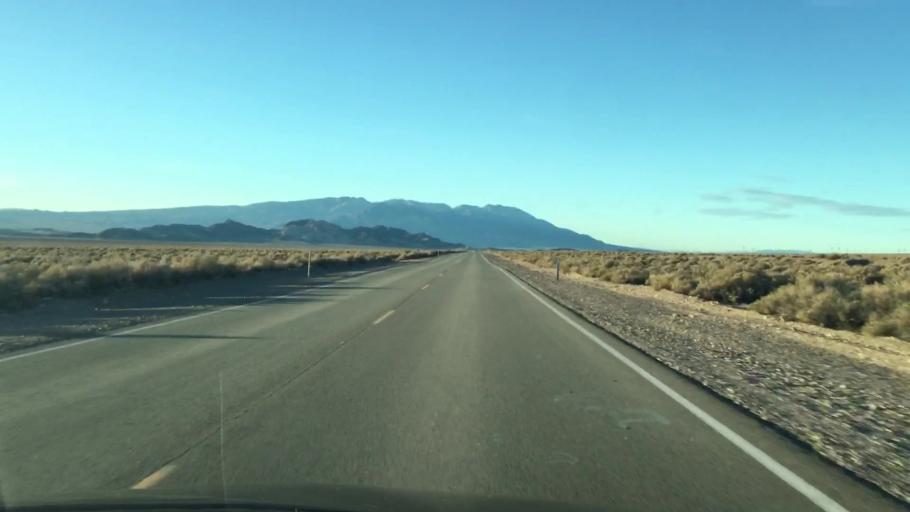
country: US
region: California
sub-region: San Bernardino County
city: Fort Irwin
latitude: 35.3497
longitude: -116.0894
